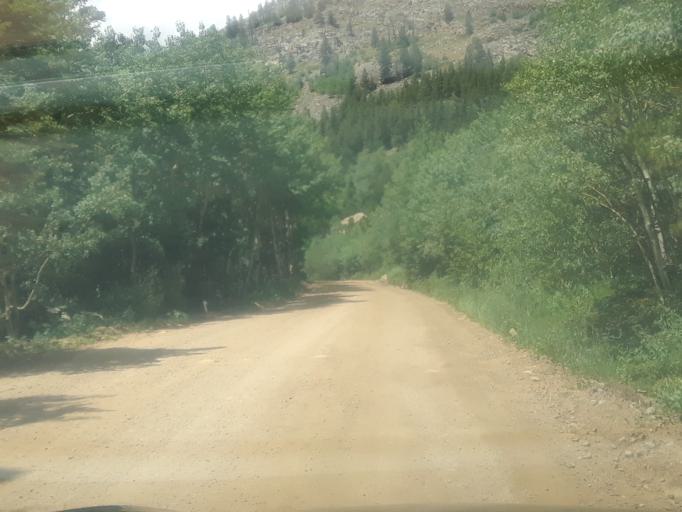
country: US
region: Colorado
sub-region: Boulder County
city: Nederland
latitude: 39.9513
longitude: -105.5839
